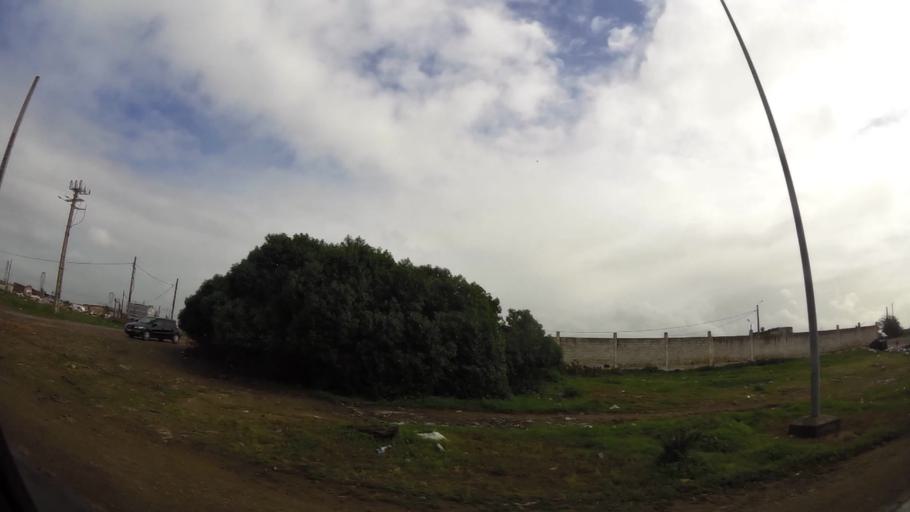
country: MA
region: Grand Casablanca
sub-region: Mohammedia
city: Mohammedia
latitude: 33.6422
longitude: -7.4276
